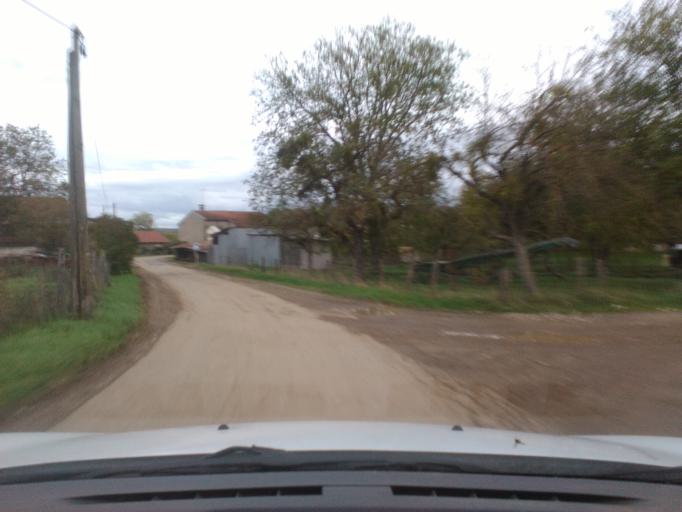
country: FR
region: Lorraine
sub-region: Departement des Vosges
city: Mirecourt
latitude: 48.3360
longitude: 6.0946
